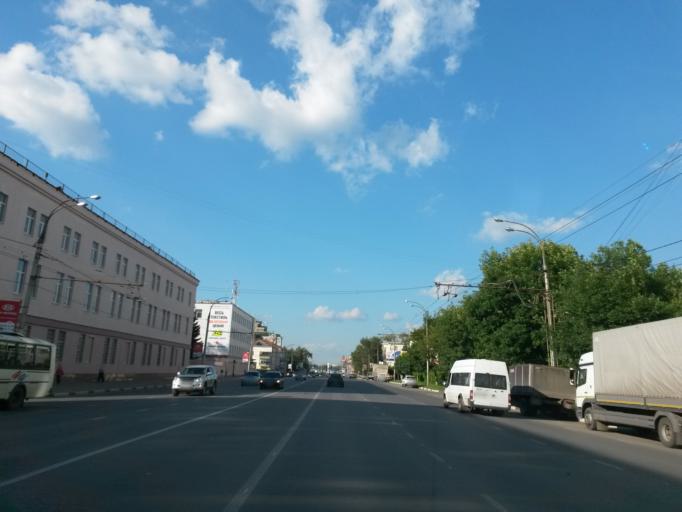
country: RU
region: Ivanovo
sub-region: Gorod Ivanovo
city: Ivanovo
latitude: 56.9765
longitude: 40.9759
